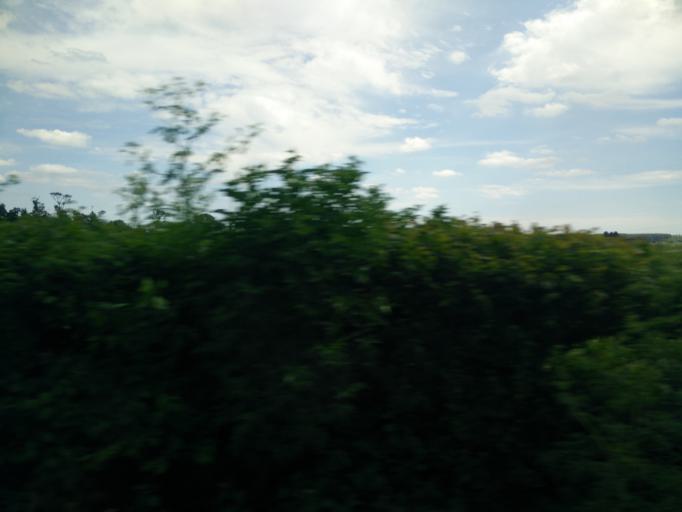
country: GB
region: England
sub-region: Cambridgeshire
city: Meldreth
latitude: 52.1068
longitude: 0.0421
